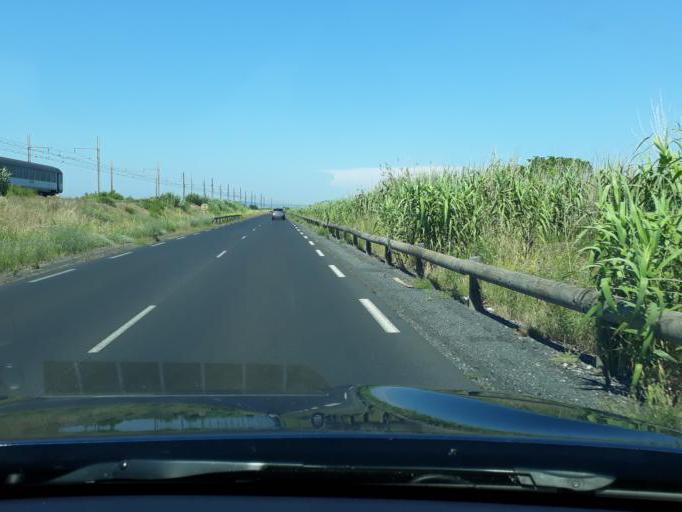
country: FR
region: Languedoc-Roussillon
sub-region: Departement de l'Herault
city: Marseillan
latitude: 43.3479
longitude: 3.5846
